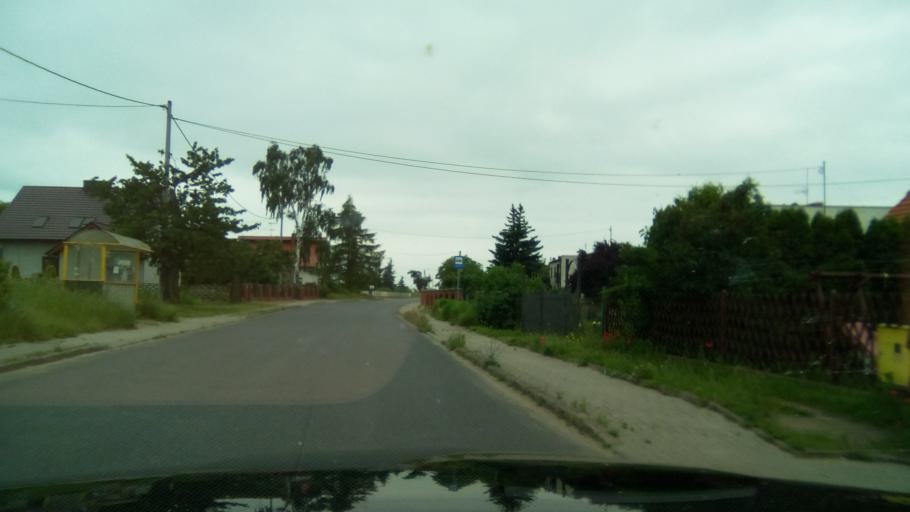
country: PL
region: Greater Poland Voivodeship
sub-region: Powiat gnieznienski
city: Gniezno
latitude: 52.5209
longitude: 17.5643
